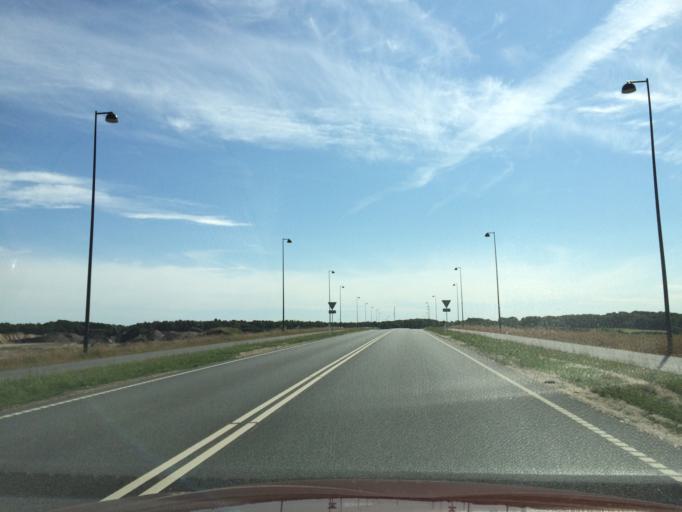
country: DK
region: Central Jutland
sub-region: Silkeborg Kommune
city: Silkeborg
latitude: 56.2032
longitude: 9.5538
